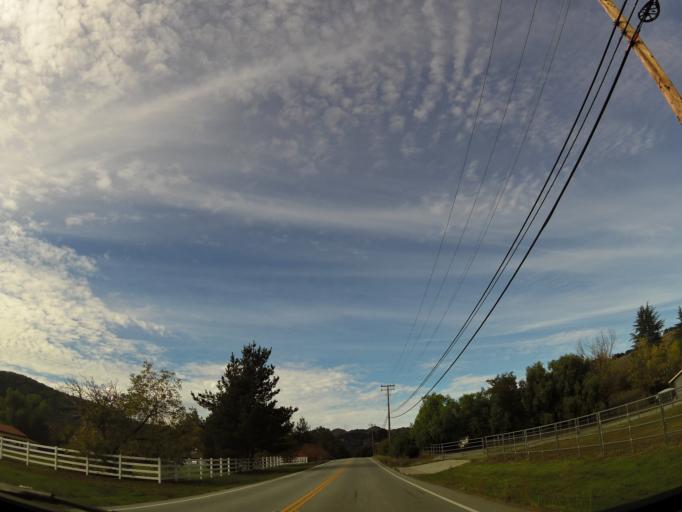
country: US
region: California
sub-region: Santa Clara County
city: San Martin
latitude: 37.0502
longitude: -121.6561
